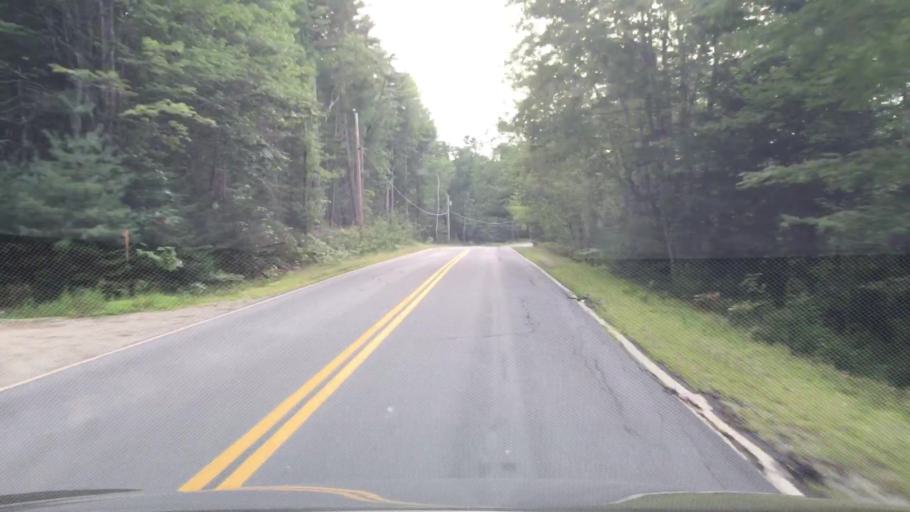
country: US
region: Maine
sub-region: Hancock County
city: Penobscot
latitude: 44.4507
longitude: -68.6911
